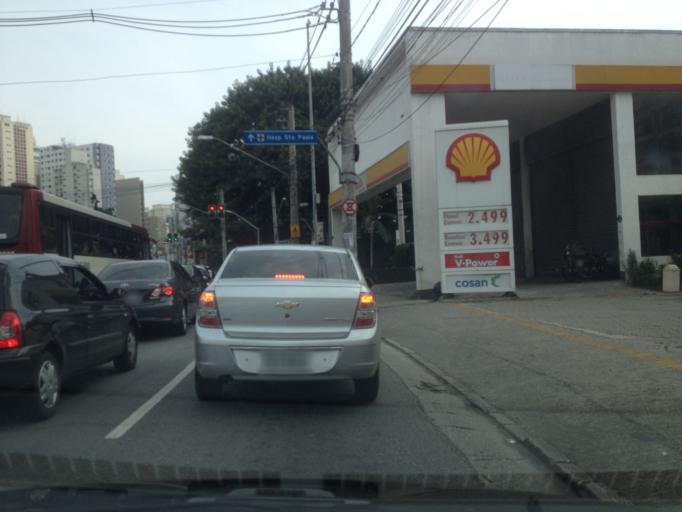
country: BR
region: Sao Paulo
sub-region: Sao Paulo
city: Sao Paulo
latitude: -23.5974
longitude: -46.6740
